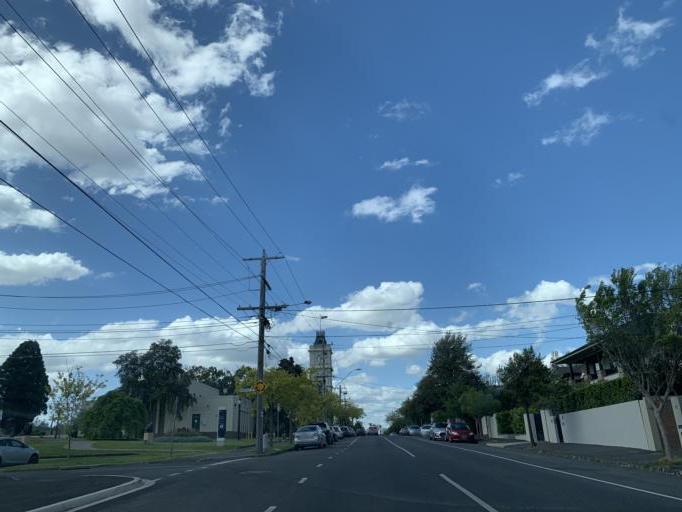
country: AU
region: Victoria
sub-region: Bayside
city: North Brighton
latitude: -37.9118
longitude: 144.9980
